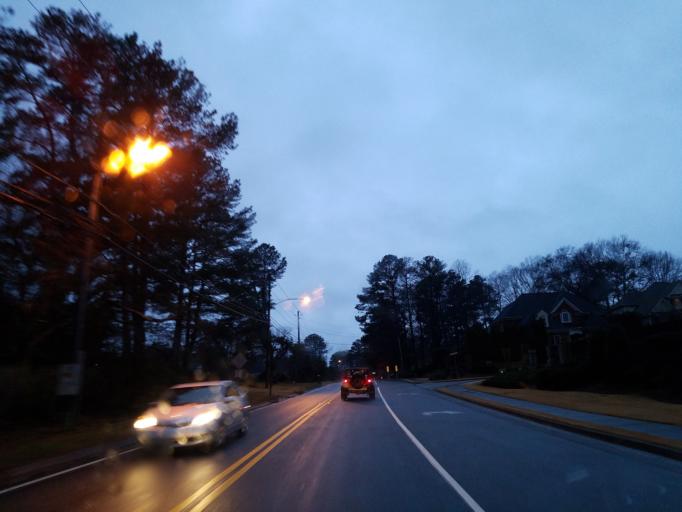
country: US
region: Georgia
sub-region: Fulton County
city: Roswell
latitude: 34.0261
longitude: -84.3390
